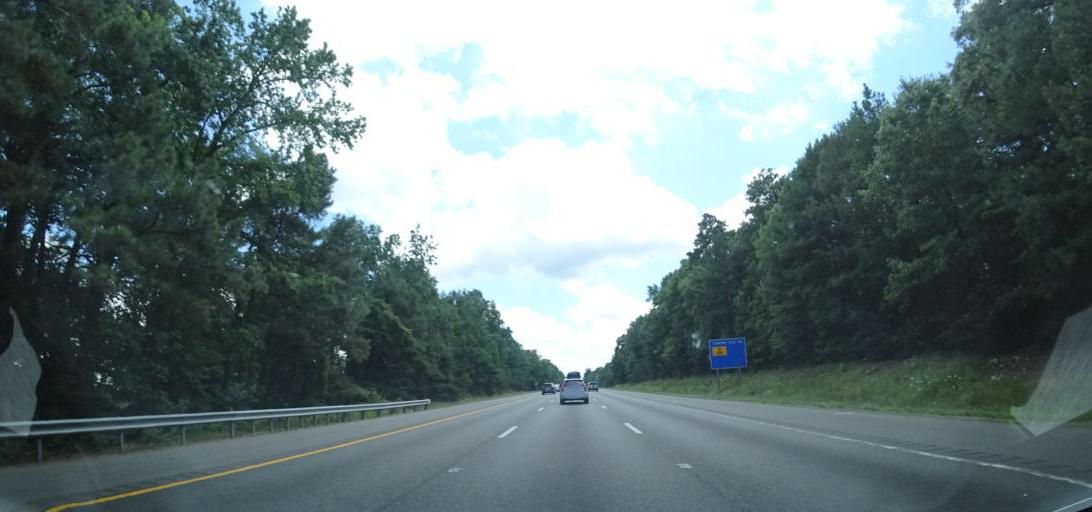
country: US
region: Virginia
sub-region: Hanover County
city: Ashland
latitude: 37.8763
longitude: -77.4554
